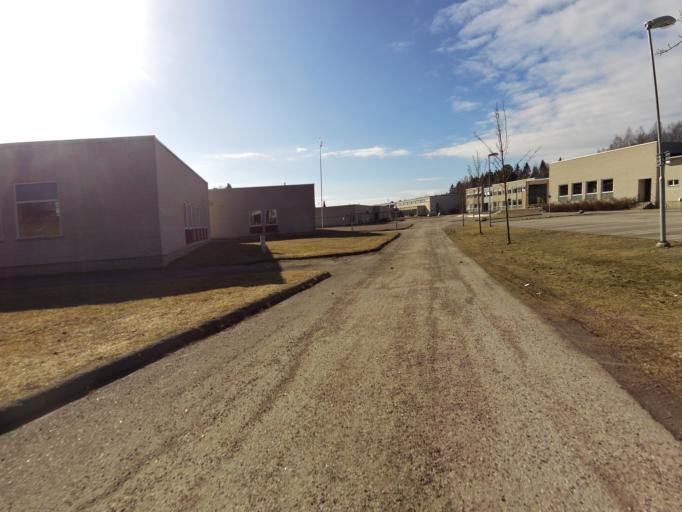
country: SE
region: Gaevleborg
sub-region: Hofors Kommun
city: Hofors
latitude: 60.5478
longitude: 16.2705
